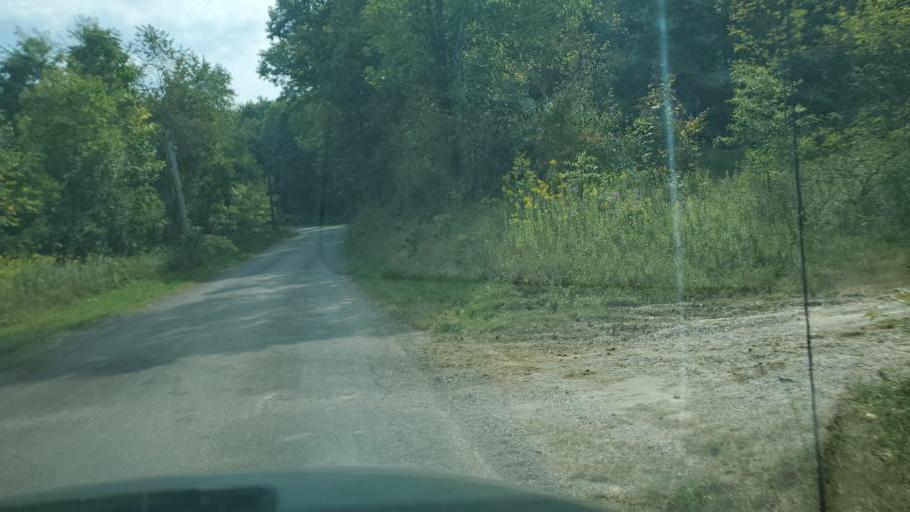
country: US
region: Ohio
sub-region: Muskingum County
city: Frazeysburg
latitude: 40.0046
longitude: -82.1942
